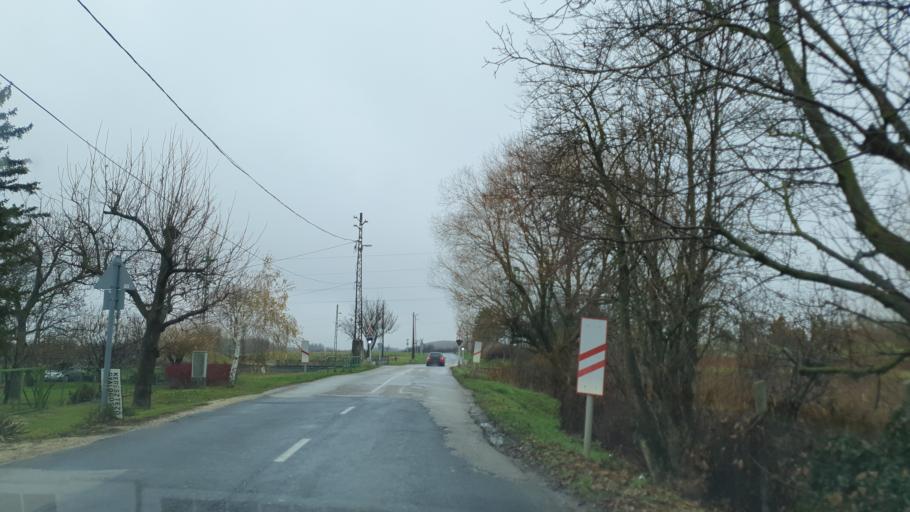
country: HU
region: Veszprem
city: Hajmasker
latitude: 47.1444
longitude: 18.0205
